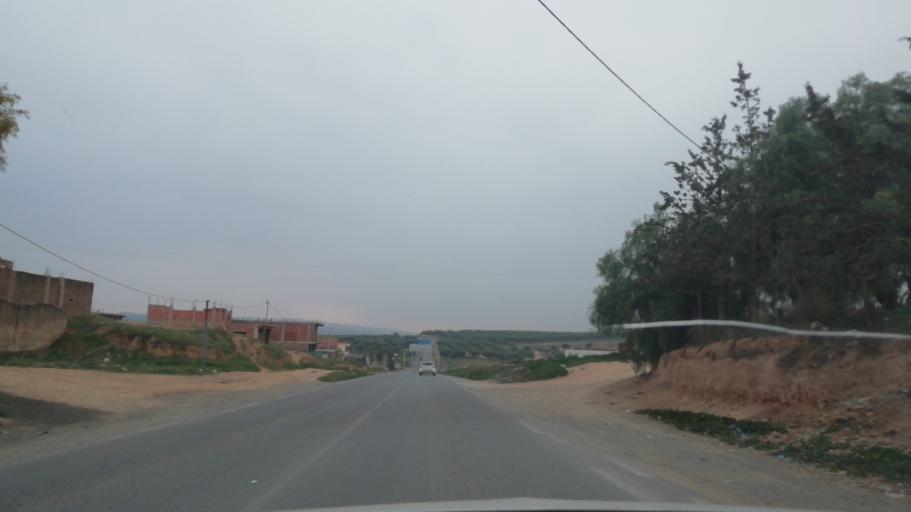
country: DZ
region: Mascara
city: Bou Hanifia el Hamamat
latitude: 35.2835
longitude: -0.1473
